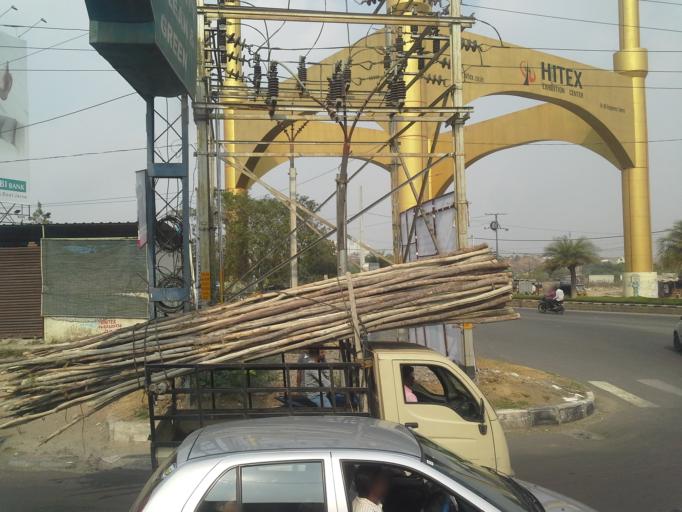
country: IN
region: Telangana
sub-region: Rangareddi
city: Kukatpalli
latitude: 17.4567
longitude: 78.3768
